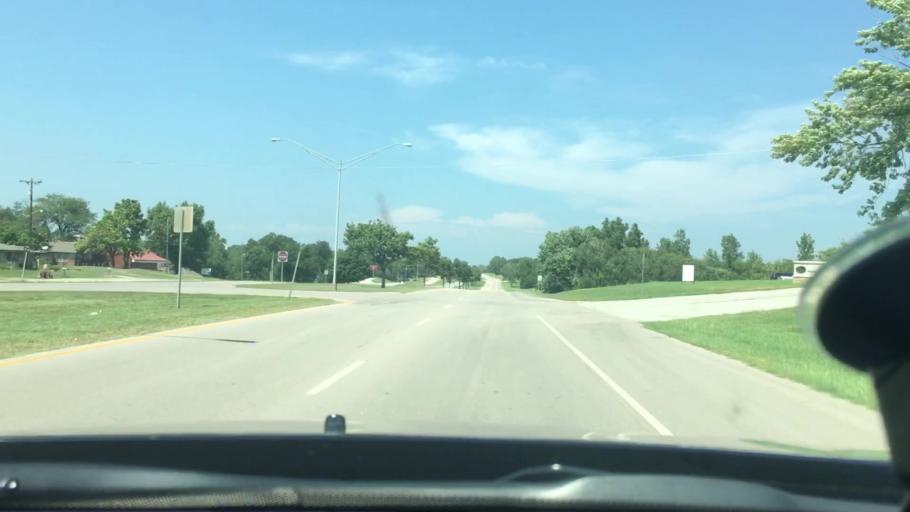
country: US
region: Oklahoma
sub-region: Pontotoc County
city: Ada
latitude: 34.8049
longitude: -96.6782
